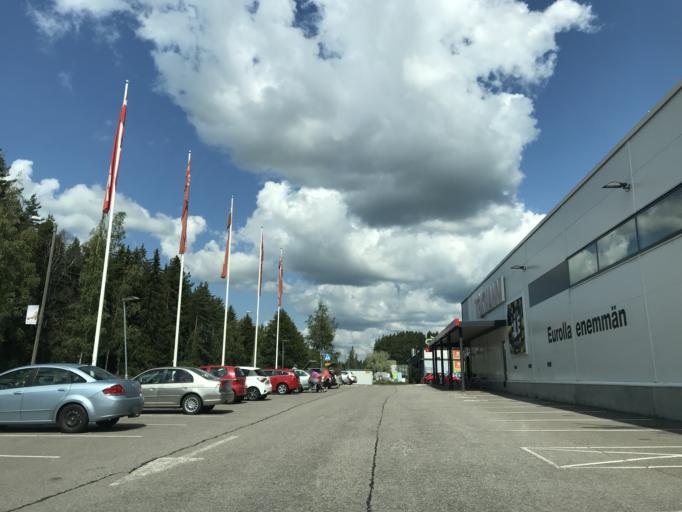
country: FI
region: Paijanne Tavastia
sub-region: Lahti
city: Orimattila
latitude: 60.8121
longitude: 25.7301
